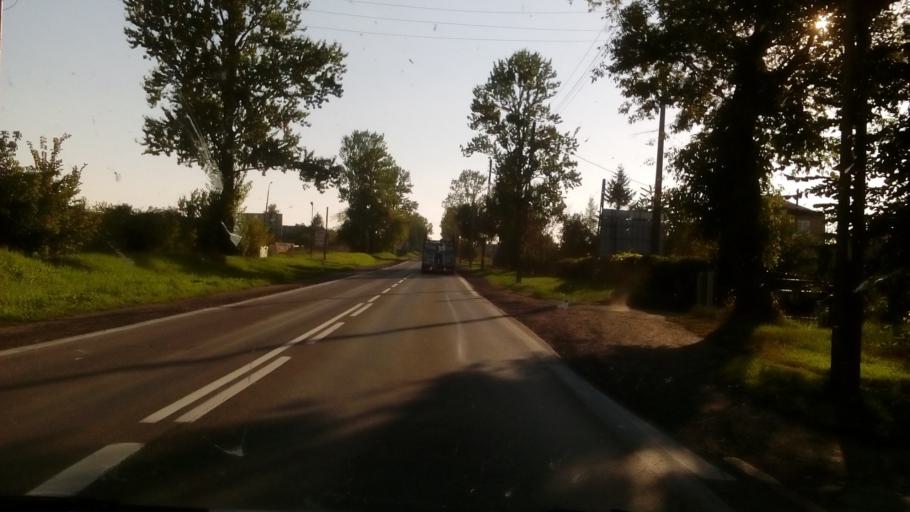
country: PL
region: Podlasie
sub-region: Powiat grajewski
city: Grajewo
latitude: 53.6427
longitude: 22.4451
